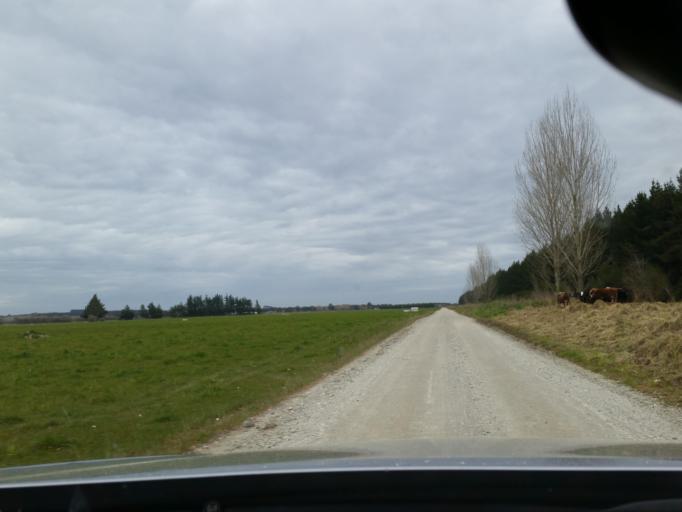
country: NZ
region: Southland
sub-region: Southland District
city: Winton
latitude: -46.2261
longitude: 168.4899
